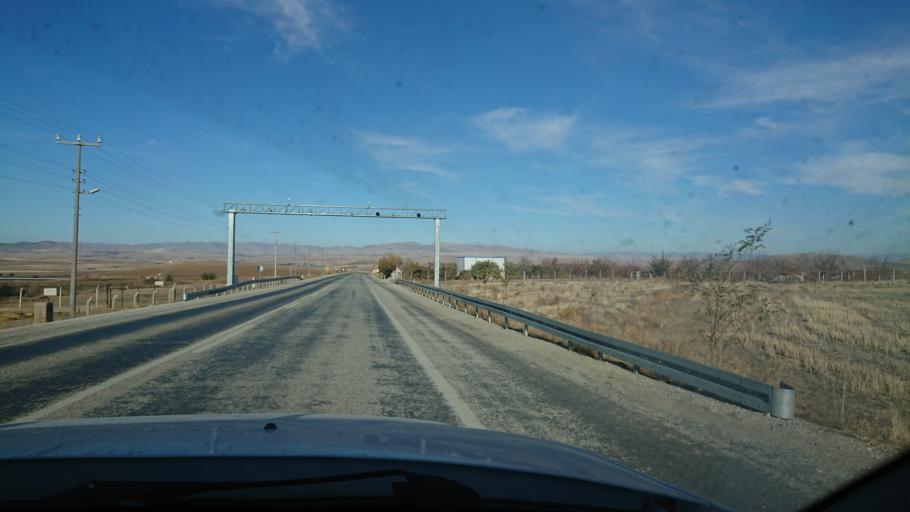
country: TR
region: Aksaray
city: Sariyahsi
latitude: 38.9937
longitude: 33.8488
